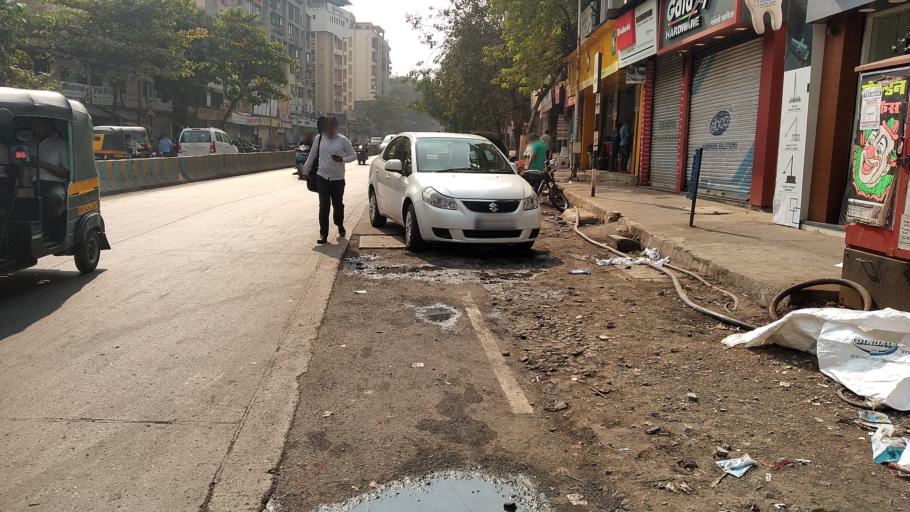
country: IN
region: Maharashtra
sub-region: Thane
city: Thane
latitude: 19.1926
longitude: 72.9696
